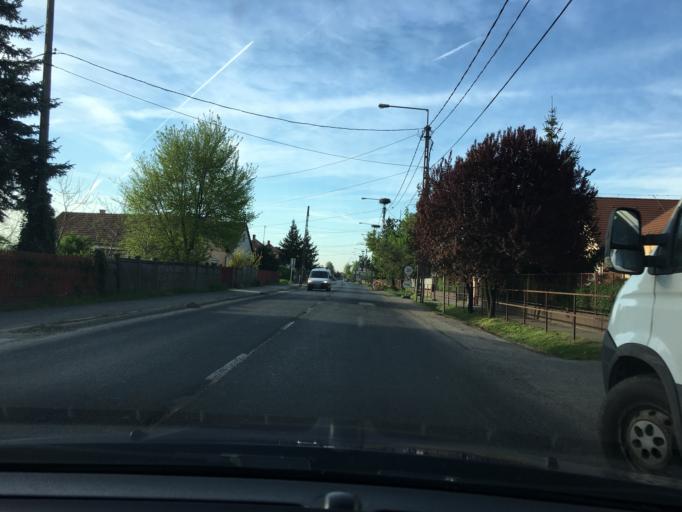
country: HU
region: Hajdu-Bihar
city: Berettyoujfalu
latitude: 47.1938
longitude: 21.5416
